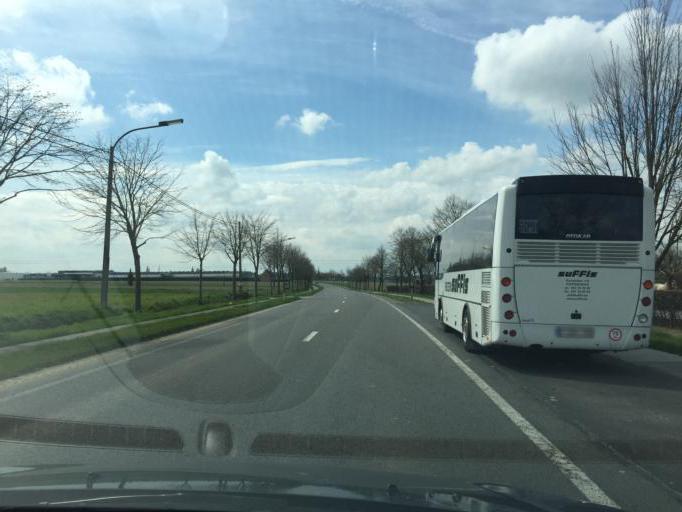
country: BE
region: Flanders
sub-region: Provincie West-Vlaanderen
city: Tielt
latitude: 51.0096
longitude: 3.3565
